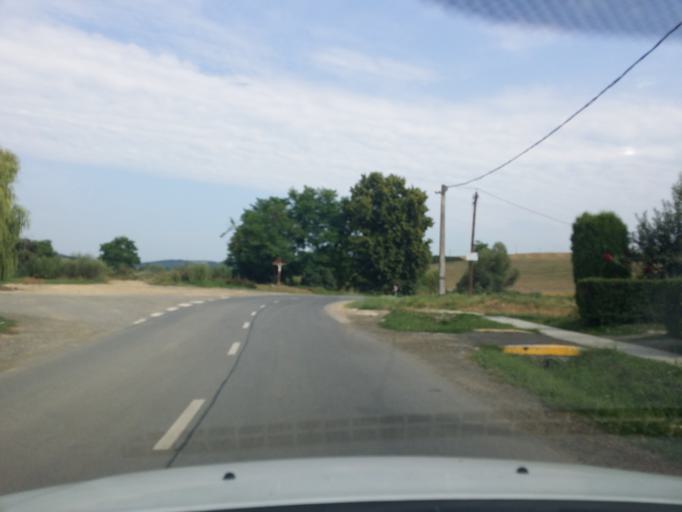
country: HU
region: Pest
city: Acsa
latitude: 47.7828
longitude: 19.3621
